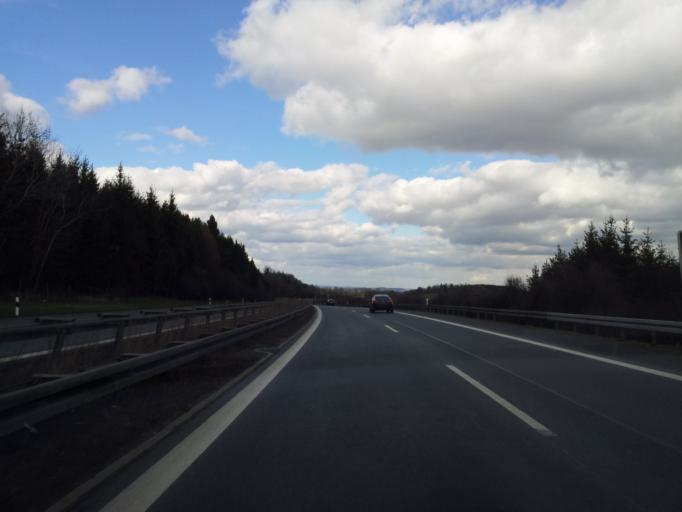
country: DE
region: Bavaria
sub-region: Upper Franconia
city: Trogen
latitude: 50.3990
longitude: 12.0123
